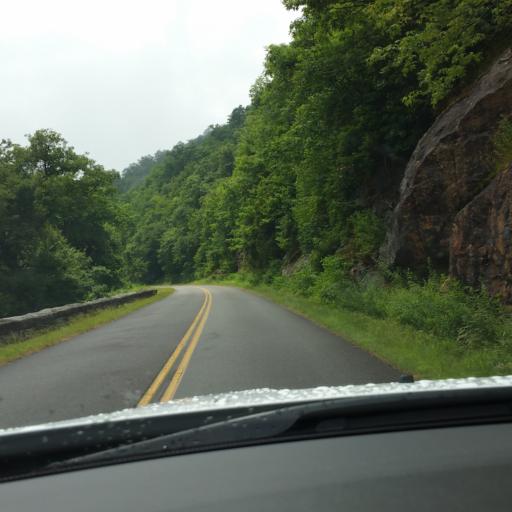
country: US
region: North Carolina
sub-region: Transylvania County
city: Brevard
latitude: 35.3633
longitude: -82.7960
